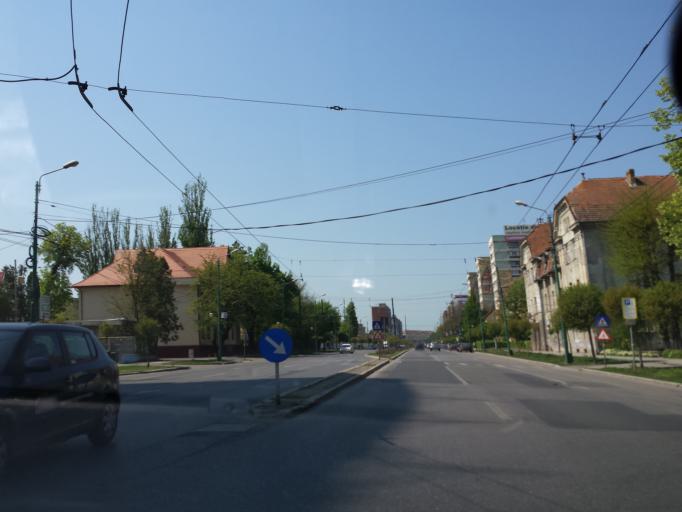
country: RO
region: Timis
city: Timisoara
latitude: 45.7621
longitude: 21.2456
